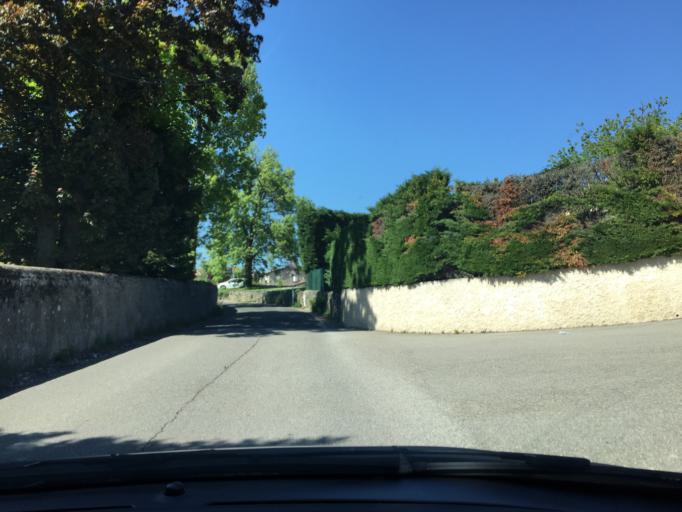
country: FR
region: Rhone-Alpes
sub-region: Departement du Rhone
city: Saint-Andeol-le-Chateau
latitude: 45.5833
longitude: 4.6976
